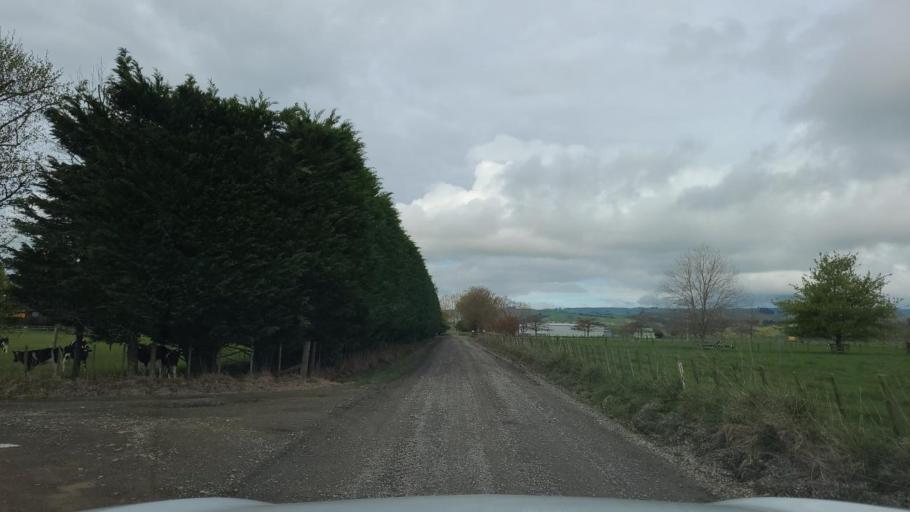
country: NZ
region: Wellington
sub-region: Masterton District
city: Masterton
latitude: -41.0795
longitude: 175.5668
